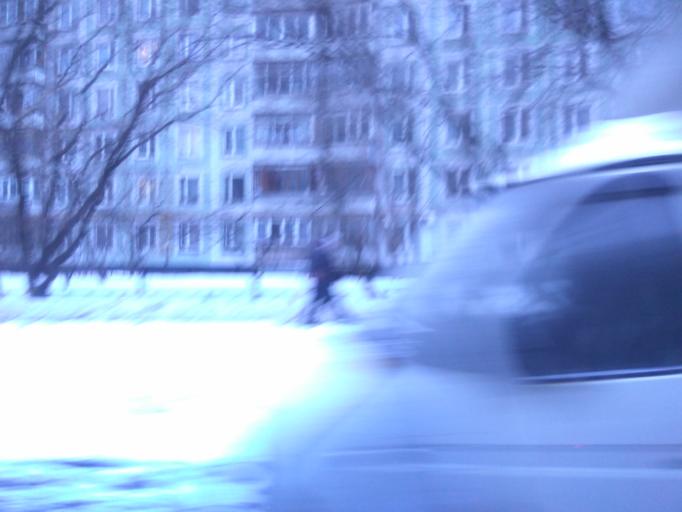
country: RU
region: Moscow
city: Gol'yanovo
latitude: 55.8163
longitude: 37.8277
